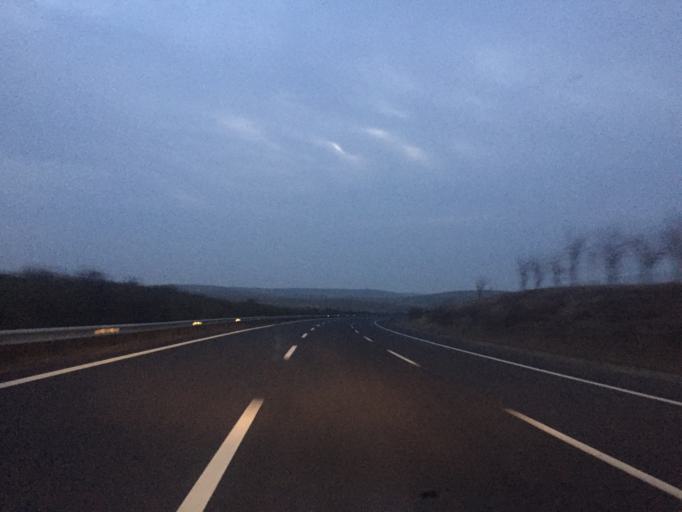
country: TR
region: Sanliurfa
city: Camlidere
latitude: 37.2016
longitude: 38.9554
